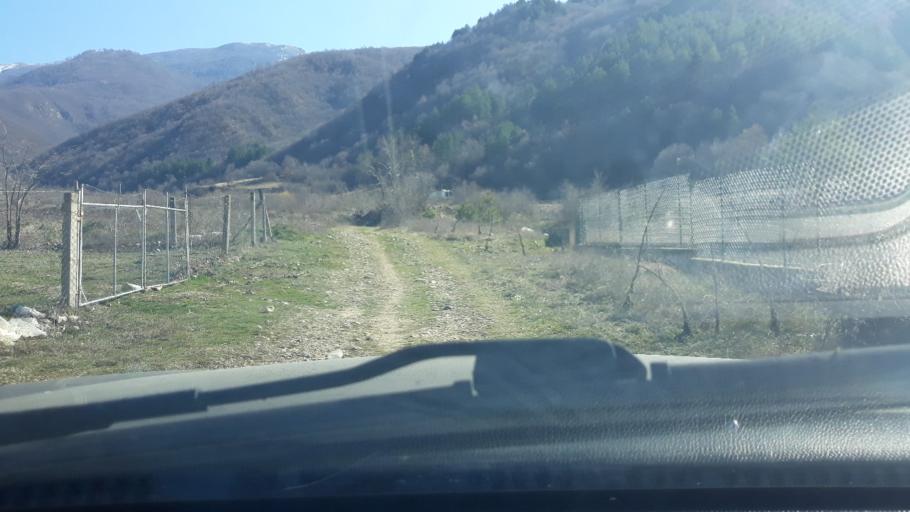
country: MK
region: Novo Selo
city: Susica
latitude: 41.3782
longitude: 22.8184
